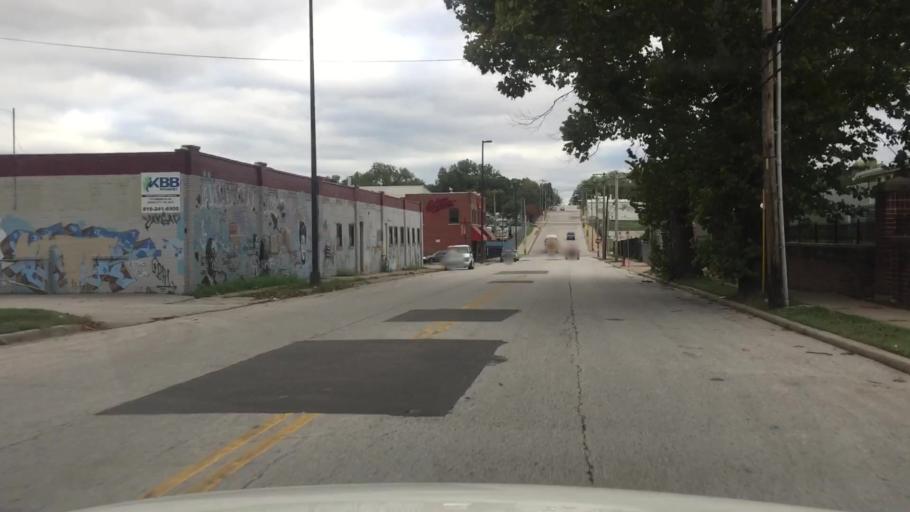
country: US
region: Missouri
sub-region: Jackson County
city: Kansas City
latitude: 39.0925
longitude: -94.5564
